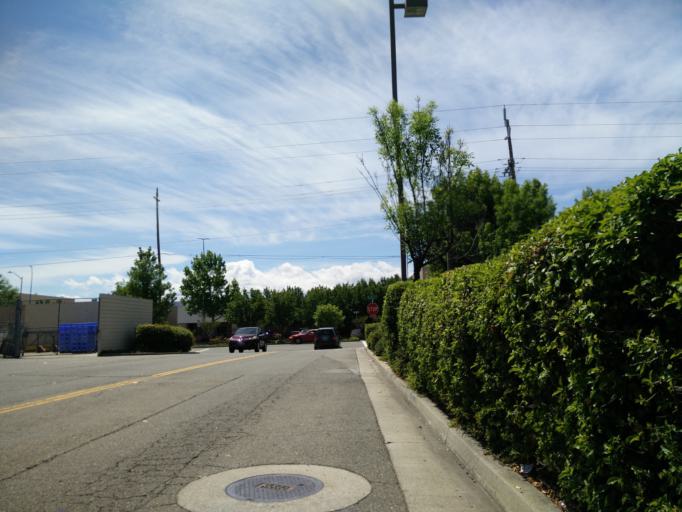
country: US
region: California
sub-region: Shasta County
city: Redding
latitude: 40.5885
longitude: -122.3526
